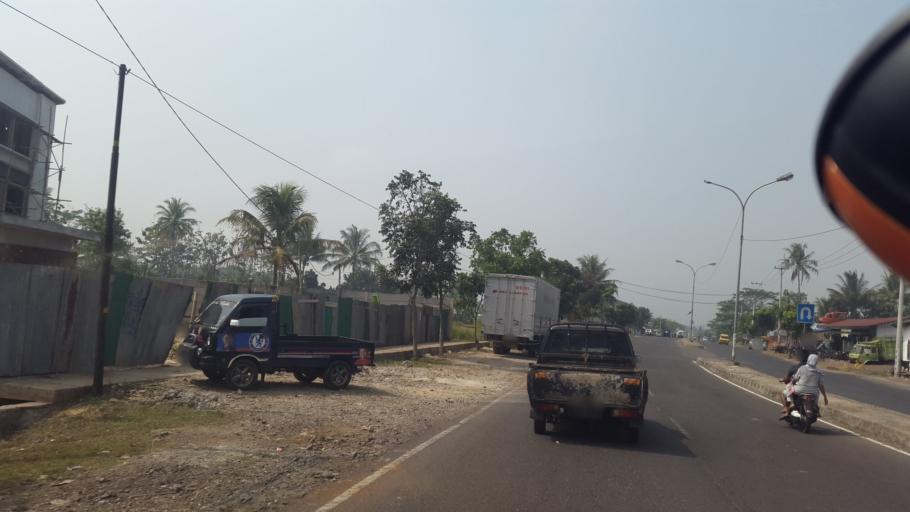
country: ID
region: West Java
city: Sukabumi
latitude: -6.9410
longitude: 106.9110
